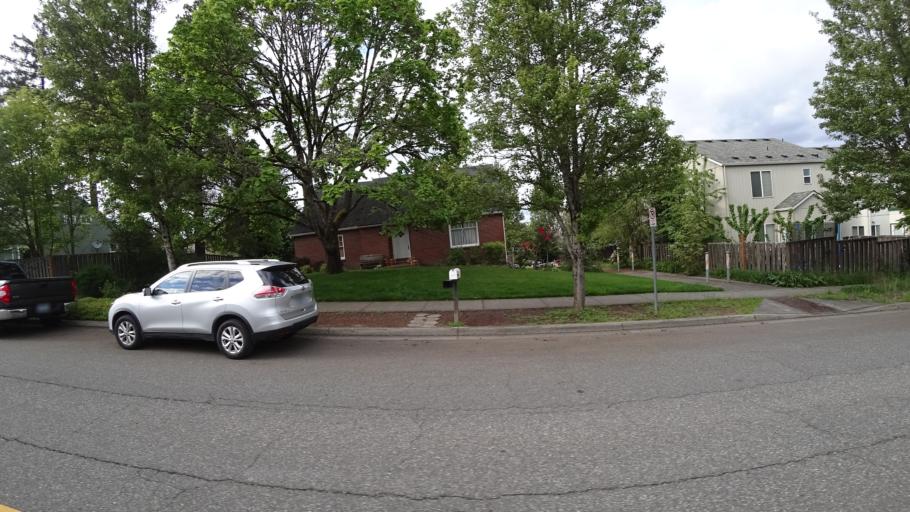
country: US
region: Oregon
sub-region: Washington County
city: Beaverton
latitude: 45.4530
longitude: -122.8377
